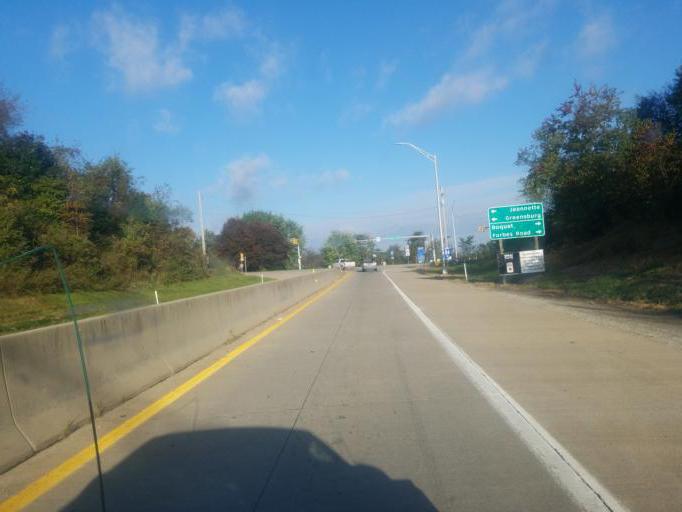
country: US
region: Pennsylvania
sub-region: Westmoreland County
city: Delmont
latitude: 40.3837
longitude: -79.5698
